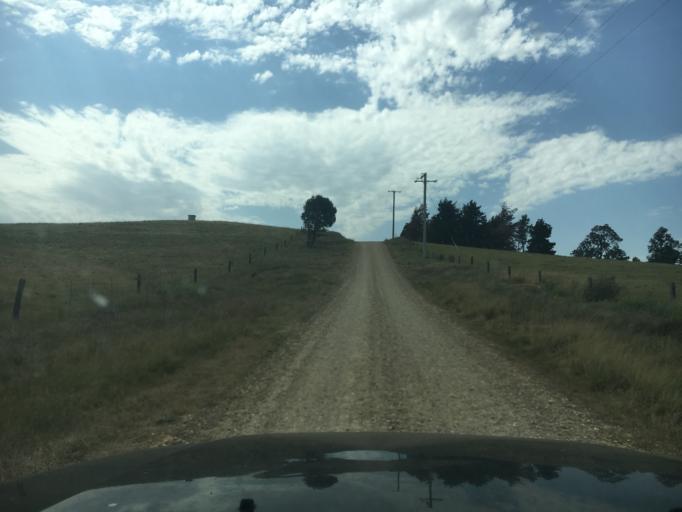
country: AU
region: New South Wales
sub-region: Cessnock
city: Branxton
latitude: -32.5065
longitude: 151.3157
